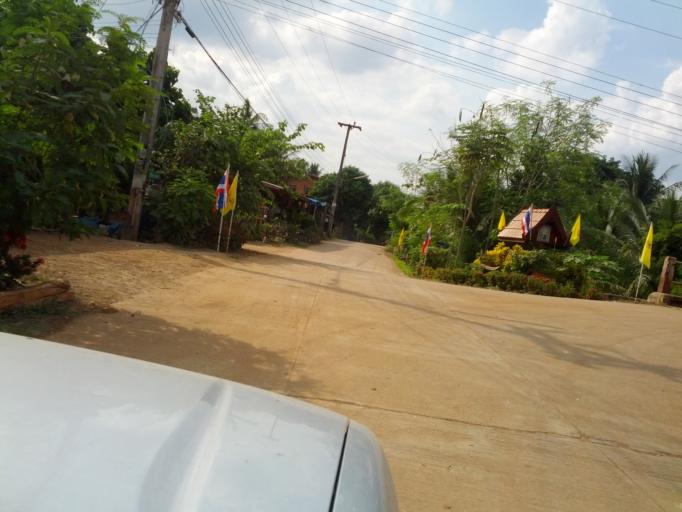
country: TH
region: Sukhothai
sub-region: Amphoe Si Satchanalai
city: Si Satchanalai
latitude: 17.4273
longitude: 99.6896
